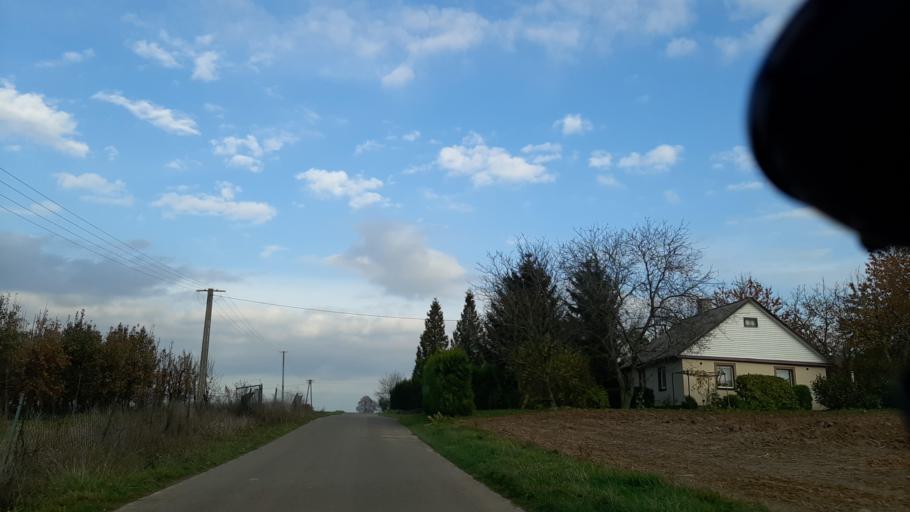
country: PL
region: Lublin Voivodeship
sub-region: Powiat pulawski
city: Markuszow
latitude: 51.3342
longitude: 22.2689
